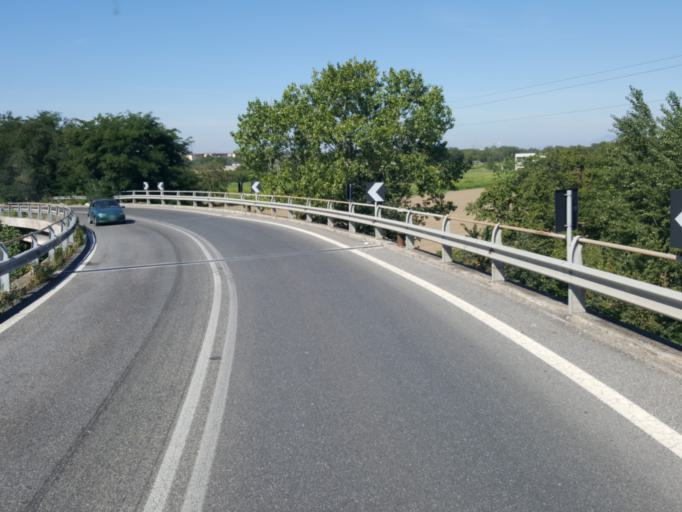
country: IT
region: Campania
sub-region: Provincia di Napoli
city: Pascarola
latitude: 40.9690
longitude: 14.2910
